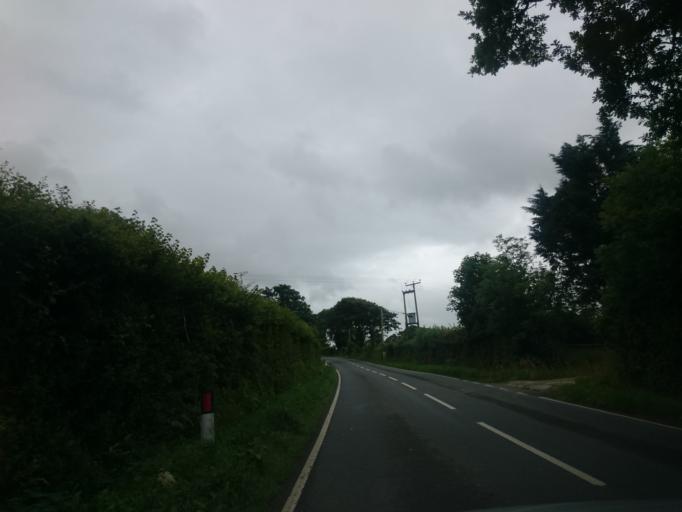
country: GB
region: Wales
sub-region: Pembrokeshire
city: Haverfordwest
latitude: 51.7819
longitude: -4.9727
